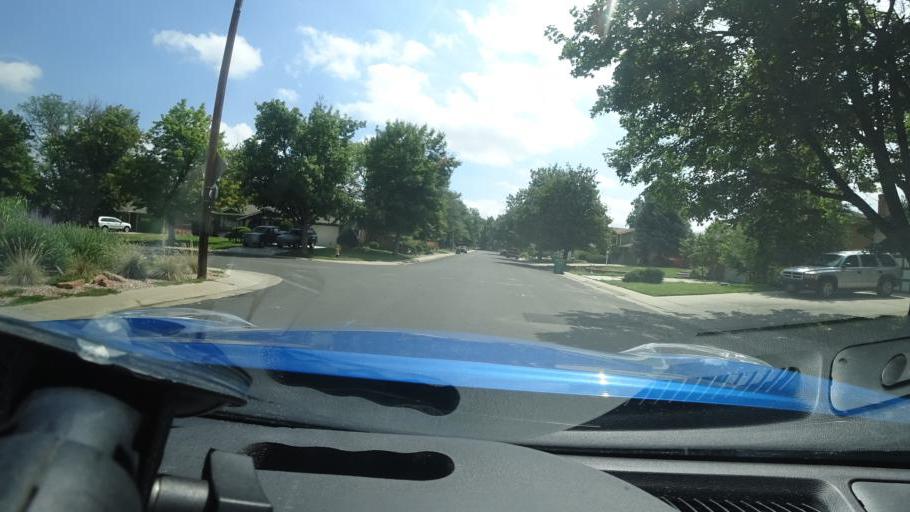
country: US
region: Colorado
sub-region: Adams County
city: Aurora
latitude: 39.7188
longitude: -104.8552
